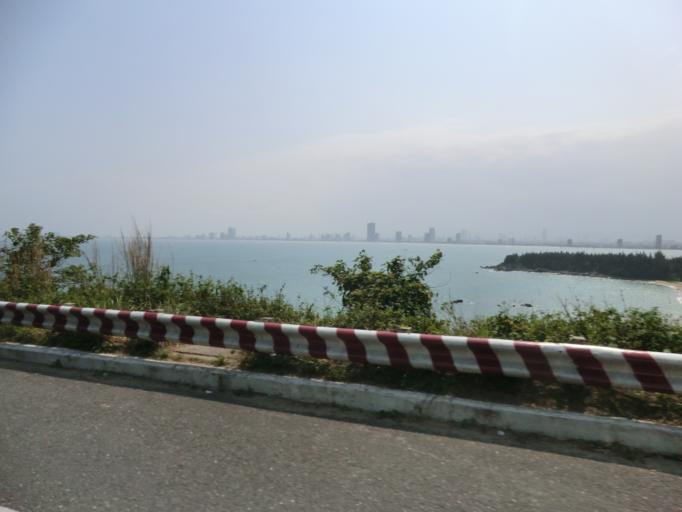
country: VN
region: Da Nang
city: Son Tra
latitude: 16.0992
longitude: 108.2758
